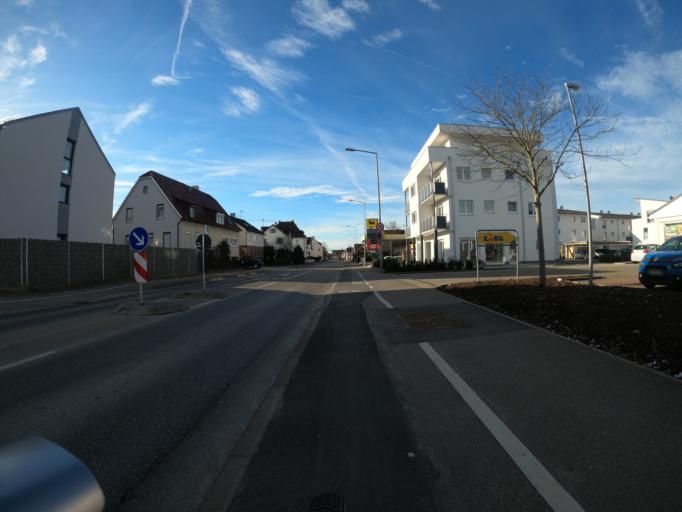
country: DE
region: Baden-Wuerttemberg
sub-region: Regierungsbezirk Stuttgart
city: Kirchheim unter Teck
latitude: 48.6552
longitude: 9.4294
